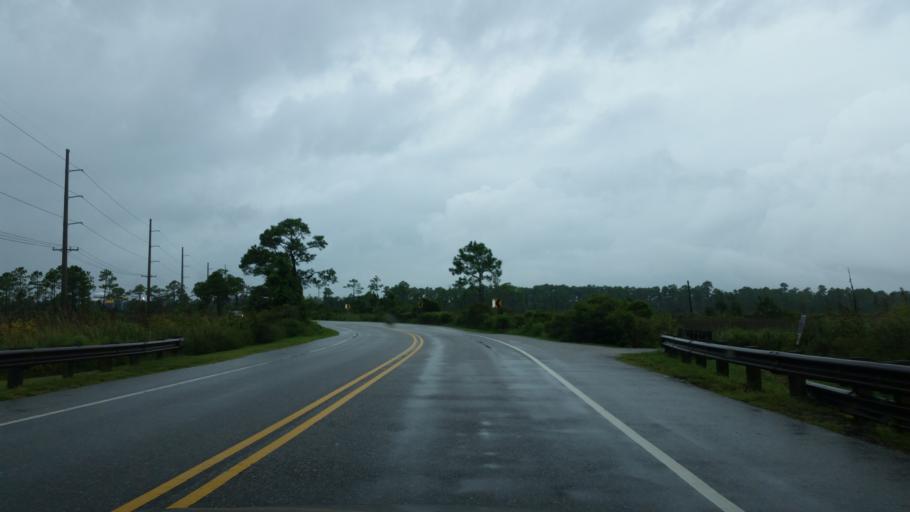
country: US
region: Alabama
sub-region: Baldwin County
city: Gulf Shores
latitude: 30.2564
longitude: -87.6790
